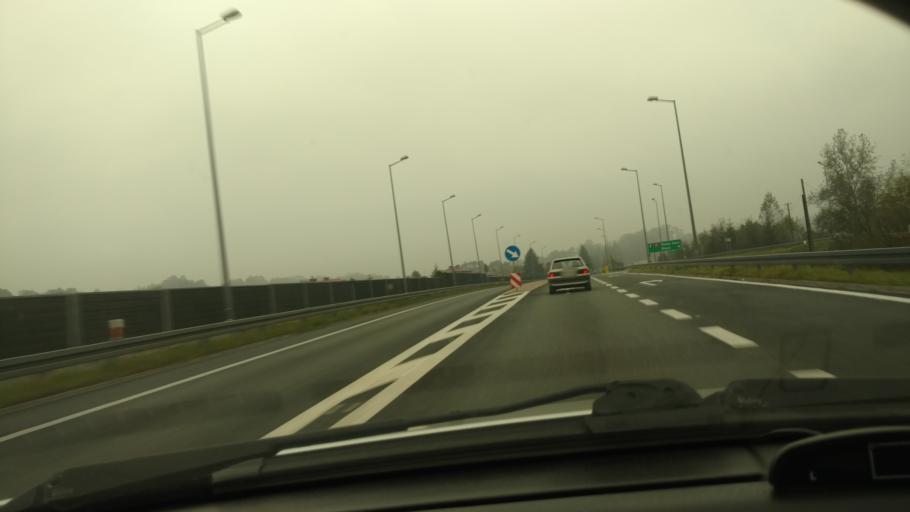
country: PL
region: Lesser Poland Voivodeship
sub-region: Powiat gorlicki
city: Biecz
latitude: 49.7087
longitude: 21.2401
